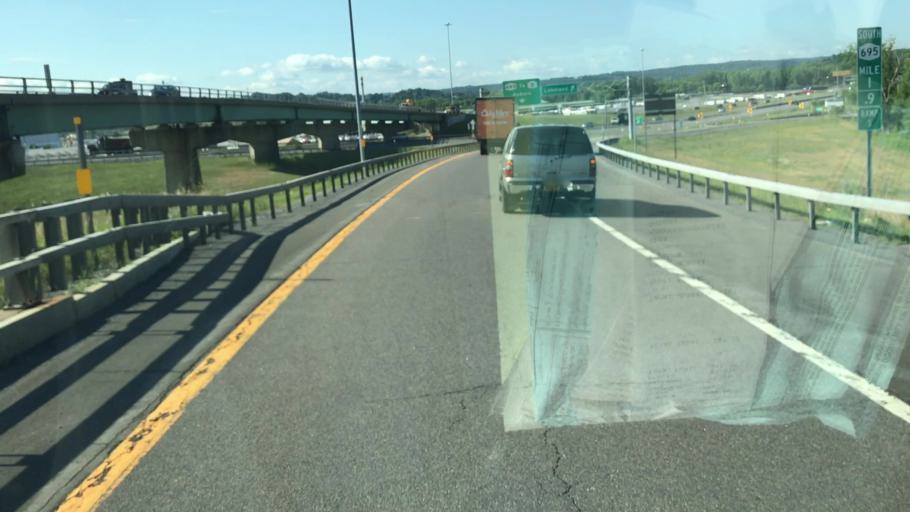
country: US
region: New York
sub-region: Onondaga County
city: Lakeland
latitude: 43.0803
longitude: -76.2261
